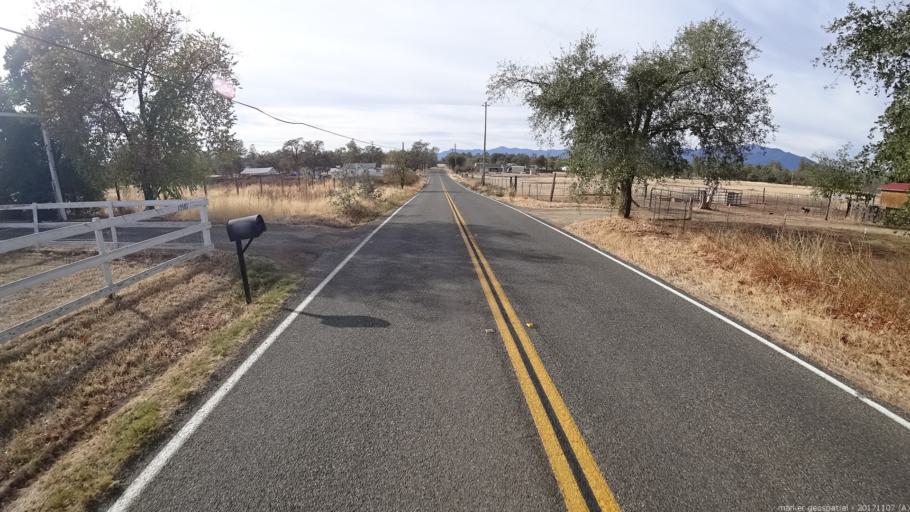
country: US
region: California
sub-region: Shasta County
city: Shasta
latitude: 40.4736
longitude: -122.4800
